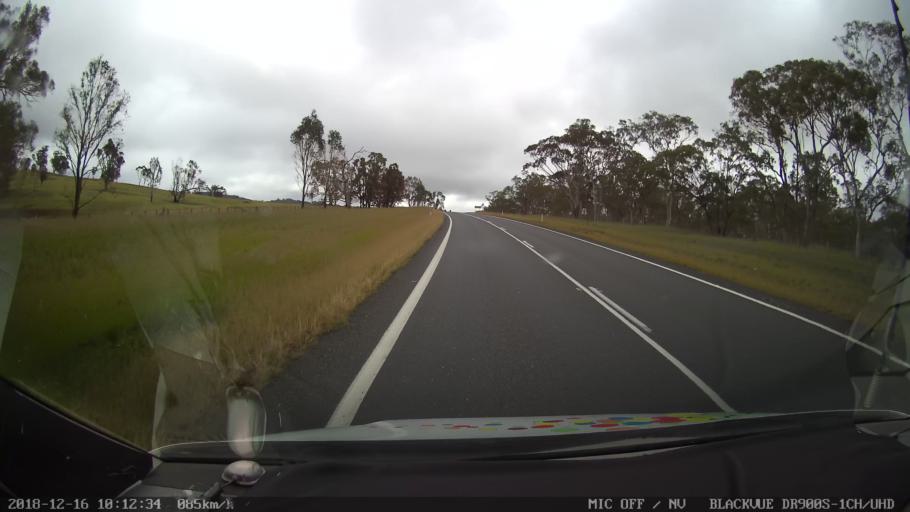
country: AU
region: New South Wales
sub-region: Glen Innes Severn
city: Glen Innes
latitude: -29.3049
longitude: 151.9423
